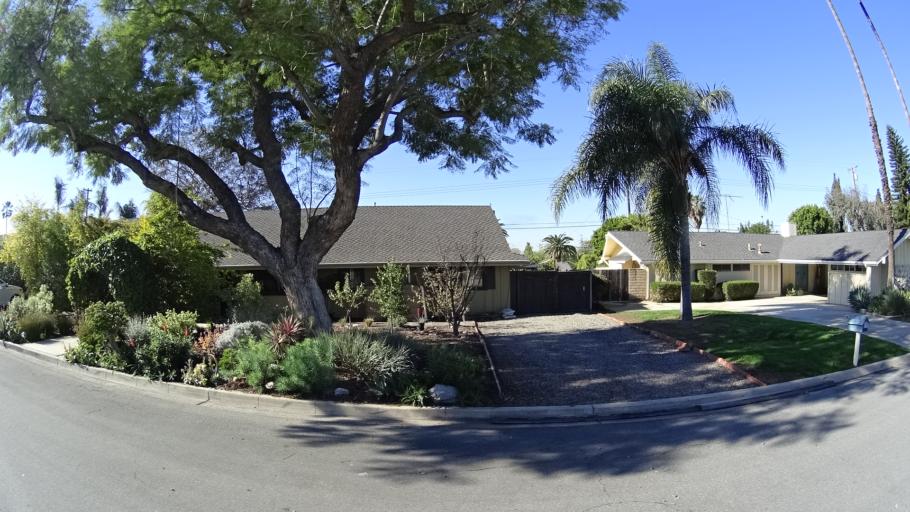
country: US
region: California
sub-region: Orange County
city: North Tustin
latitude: 33.7723
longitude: -117.8088
